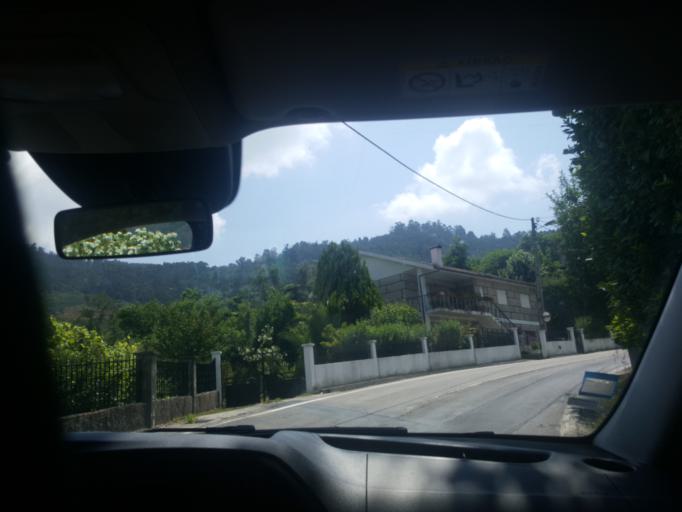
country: PT
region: Porto
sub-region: Amarante
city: Amarante
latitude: 41.2472
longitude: -8.0342
